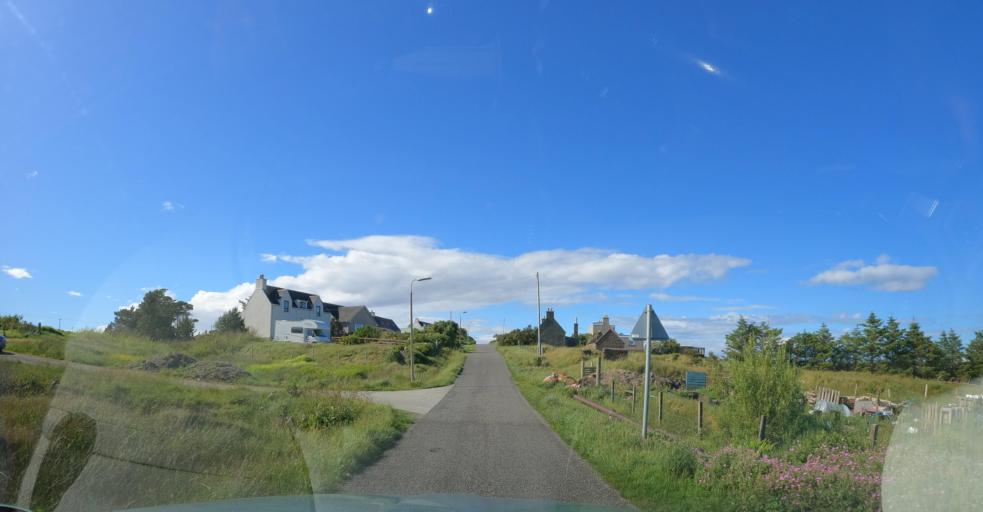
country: GB
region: Scotland
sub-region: Eilean Siar
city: Stornoway
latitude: 58.1951
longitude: -6.2230
